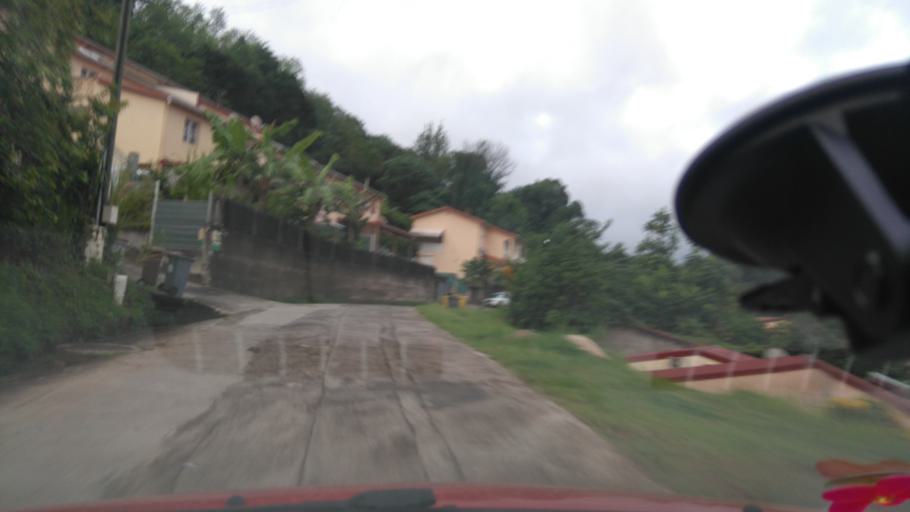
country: MQ
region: Martinique
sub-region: Martinique
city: Saint-Esprit
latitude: 14.5642
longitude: -60.9334
